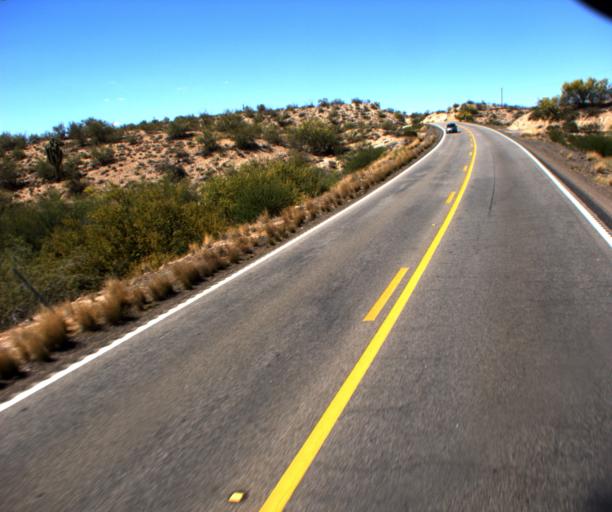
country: US
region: Arizona
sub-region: Yavapai County
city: Bagdad
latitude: 34.7923
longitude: -113.6232
